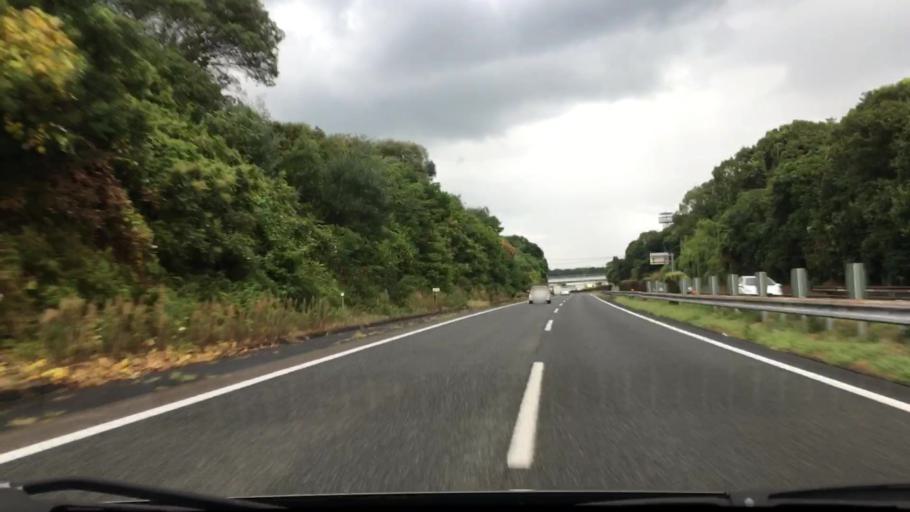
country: JP
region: Fukuoka
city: Miyata
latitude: 33.7467
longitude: 130.6155
